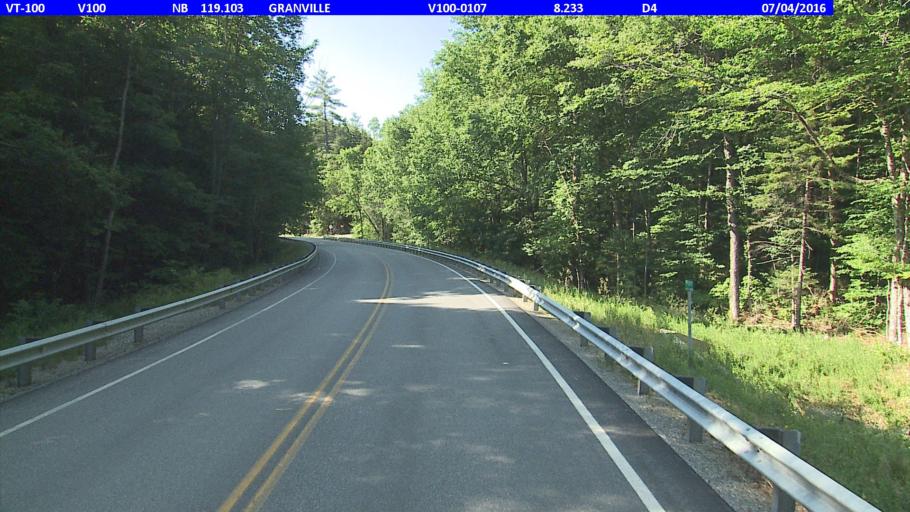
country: US
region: Vermont
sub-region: Washington County
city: Northfield
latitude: 44.0487
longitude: -72.8299
